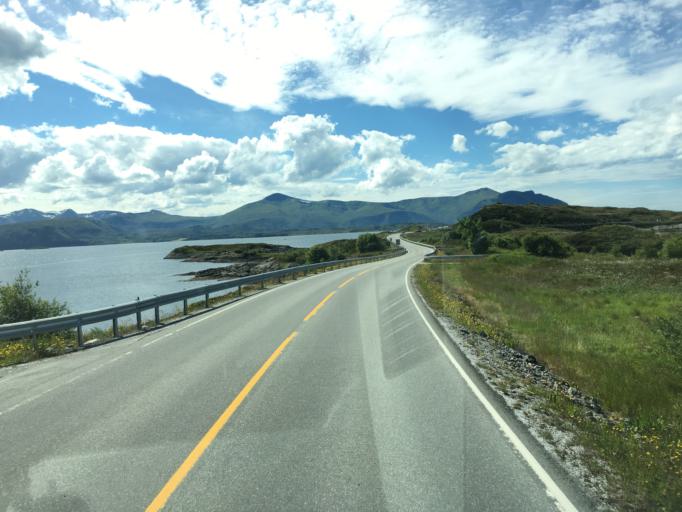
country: NO
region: More og Romsdal
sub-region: Eide
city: Eide
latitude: 63.0208
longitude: 7.3728
